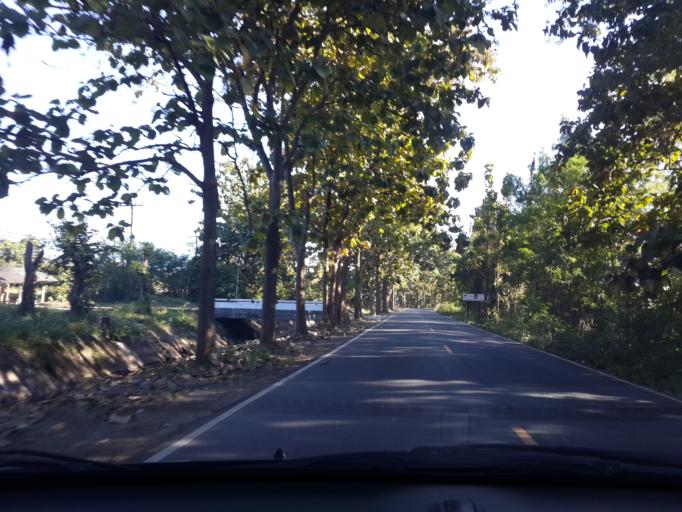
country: TH
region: Chiang Mai
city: San Sai
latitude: 18.8937
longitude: 99.1407
